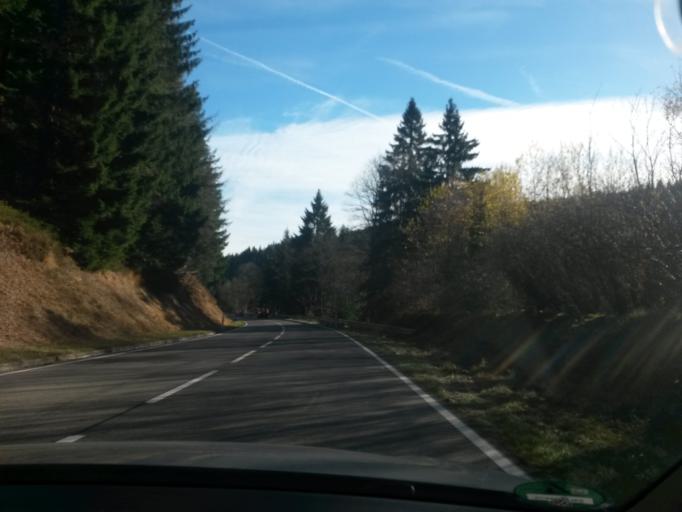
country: DE
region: Baden-Wuerttemberg
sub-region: Karlsruhe Region
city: Freudenstadt
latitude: 48.4579
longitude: 8.3750
